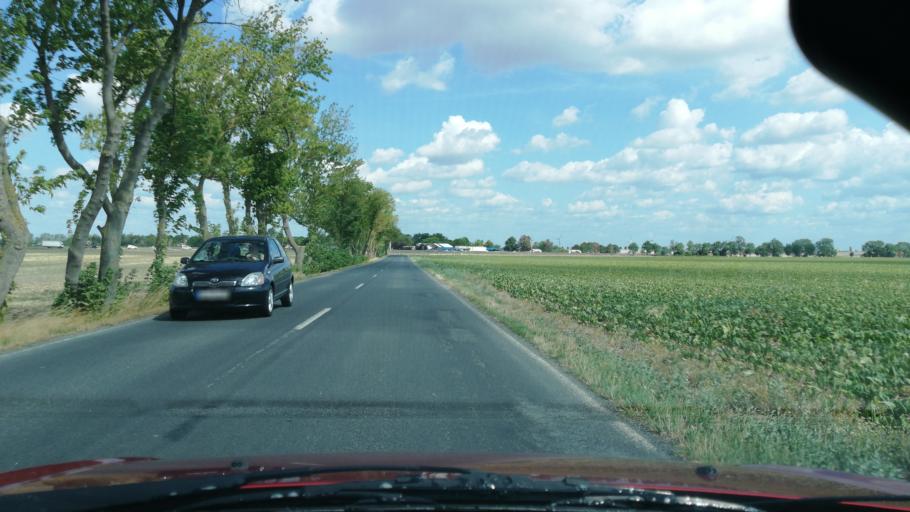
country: DE
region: Saxony-Anhalt
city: Landsberg
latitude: 51.5309
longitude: 12.1368
